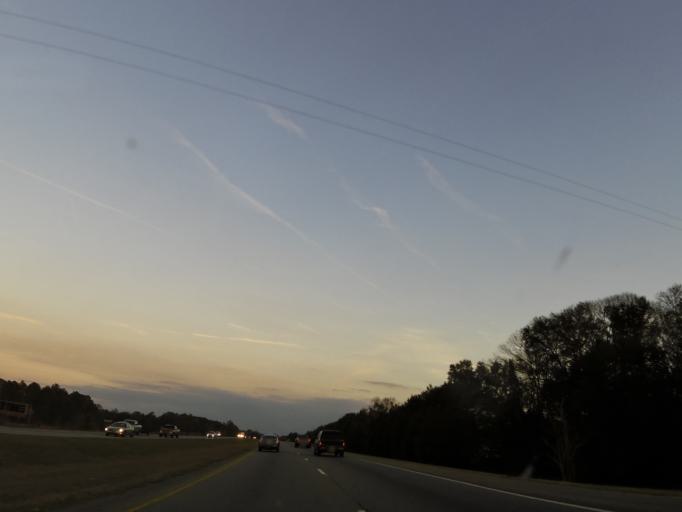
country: US
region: Georgia
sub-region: Dougherty County
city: Albany
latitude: 31.5951
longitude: -84.1373
